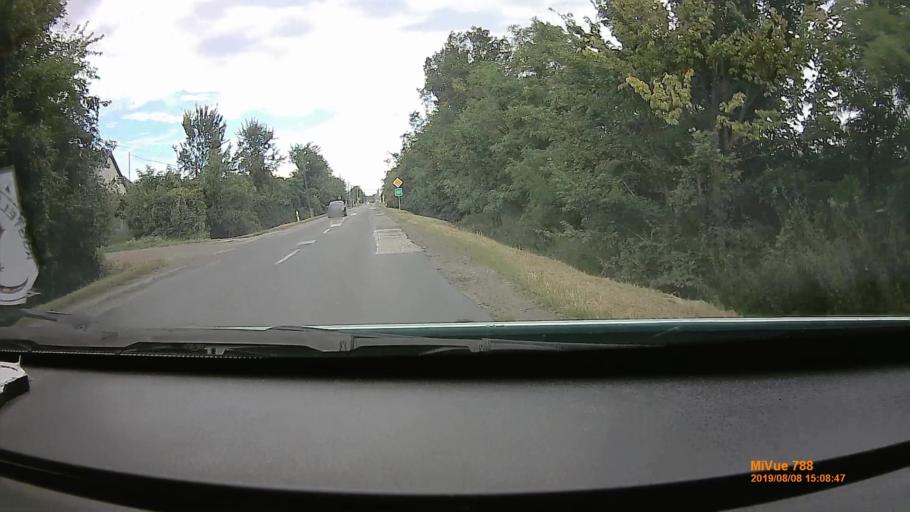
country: HU
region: Szabolcs-Szatmar-Bereg
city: Tunyogmatolcs
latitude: 47.9600
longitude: 22.4426
